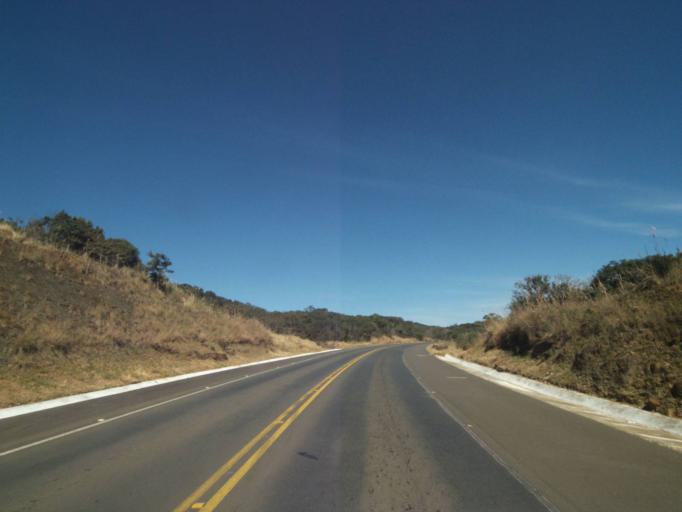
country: BR
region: Parana
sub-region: Tibagi
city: Tibagi
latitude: -24.7809
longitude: -50.4649
